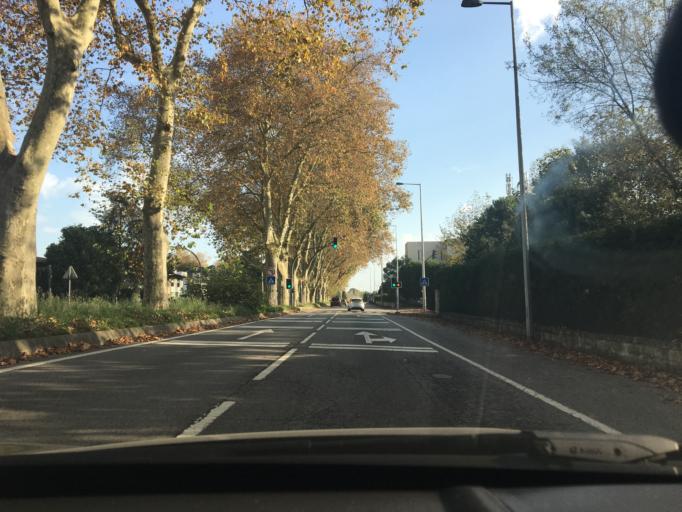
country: PT
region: Porto
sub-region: Matosinhos
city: Senhora da Hora
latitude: 41.1785
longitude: -8.6635
